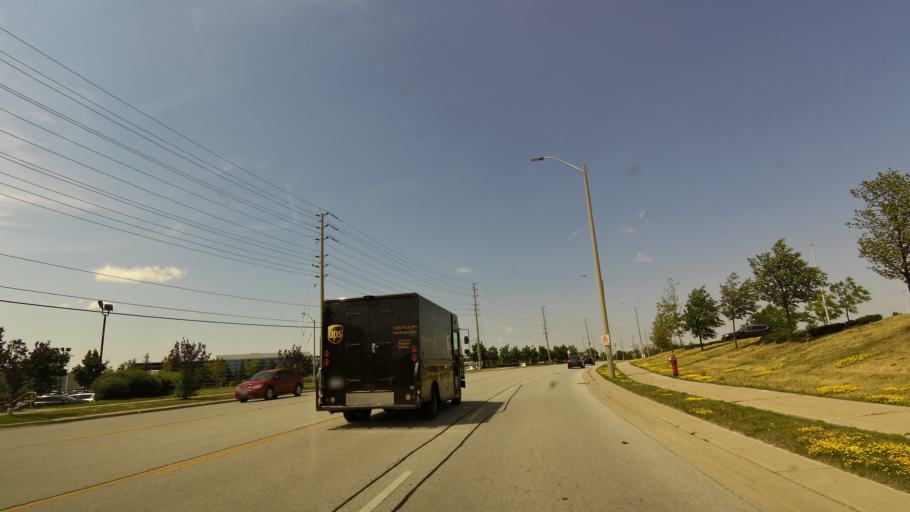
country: CA
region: Ontario
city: Etobicoke
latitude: 43.6422
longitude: -79.6153
